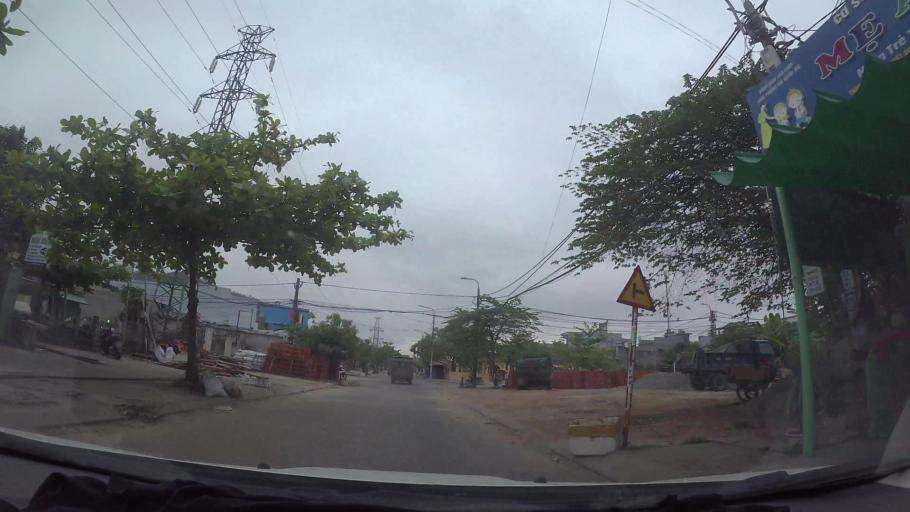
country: VN
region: Da Nang
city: Lien Chieu
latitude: 16.0688
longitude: 108.1456
